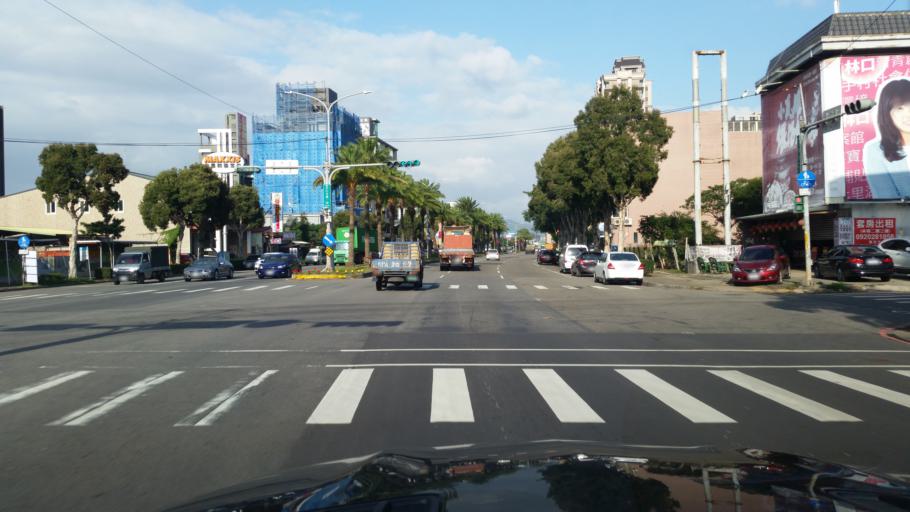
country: TW
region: Taiwan
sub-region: Taoyuan
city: Taoyuan
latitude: 25.0702
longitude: 121.3574
